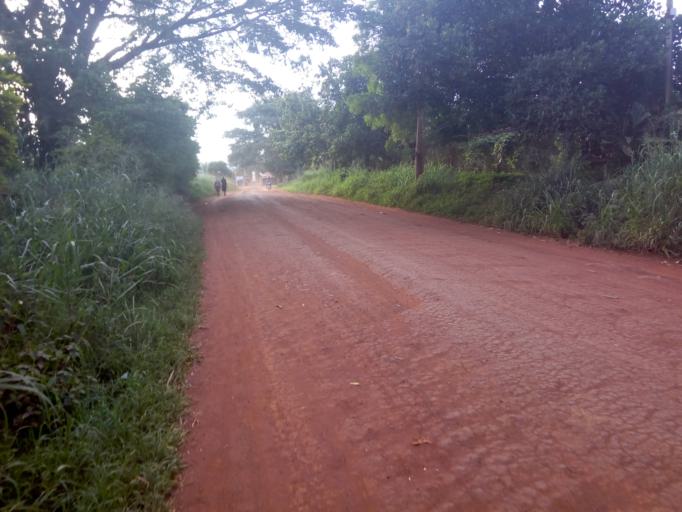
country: UG
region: Western Region
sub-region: Masindi District
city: Masindi
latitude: 1.6857
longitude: 31.7172
